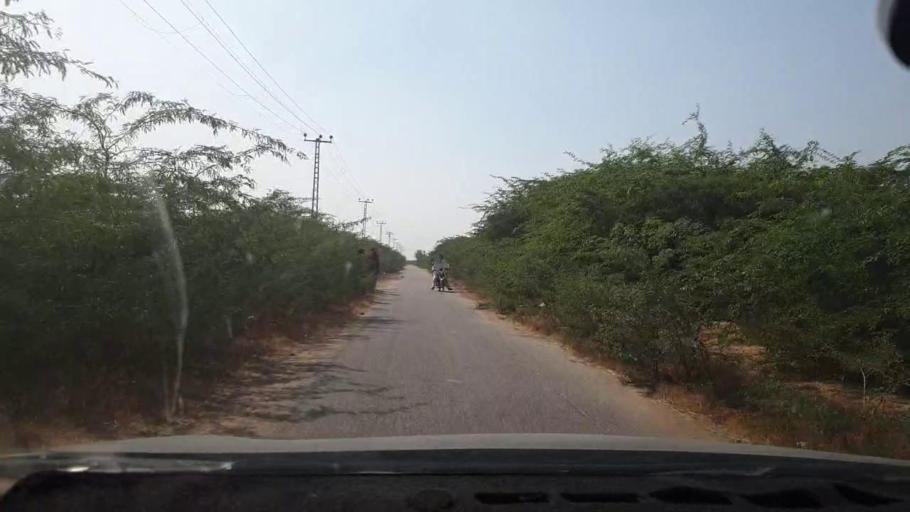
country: PK
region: Sindh
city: Malir Cantonment
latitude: 25.1154
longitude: 67.2103
